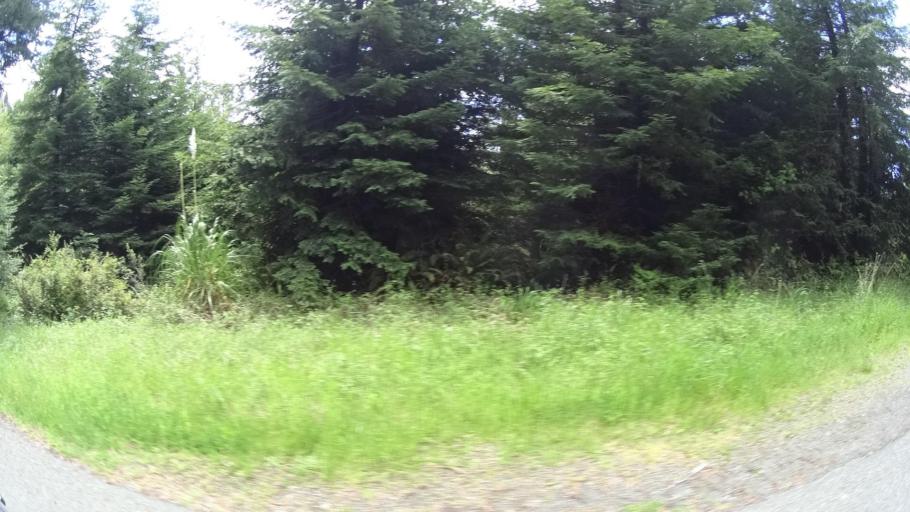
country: US
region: California
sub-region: Humboldt County
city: Blue Lake
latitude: 40.8473
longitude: -123.9256
